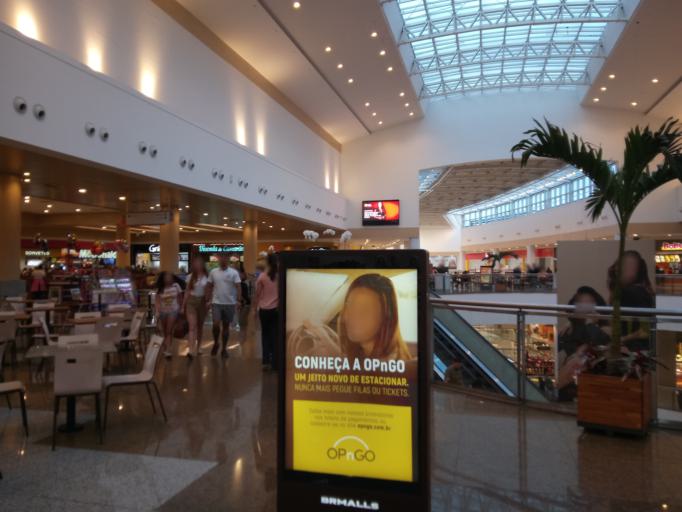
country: BR
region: Sao Paulo
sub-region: Sao Bernardo Do Campo
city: Sao Bernardo do Campo
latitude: -23.7234
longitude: -46.5432
